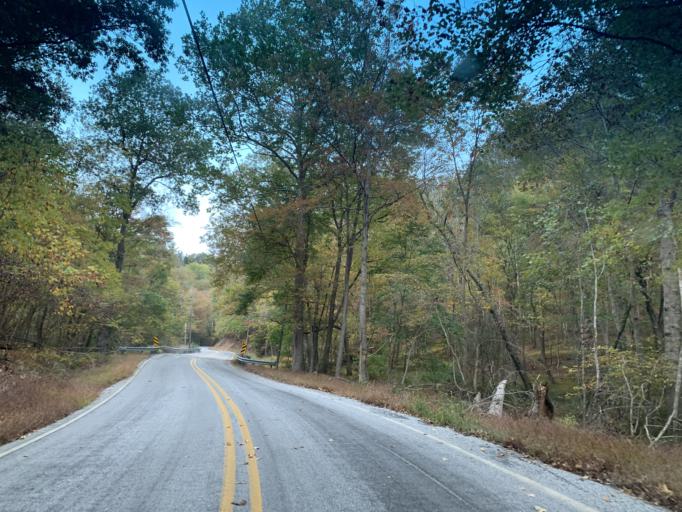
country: US
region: Pennsylvania
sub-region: York County
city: Windsor
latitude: 39.8325
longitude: -76.5142
